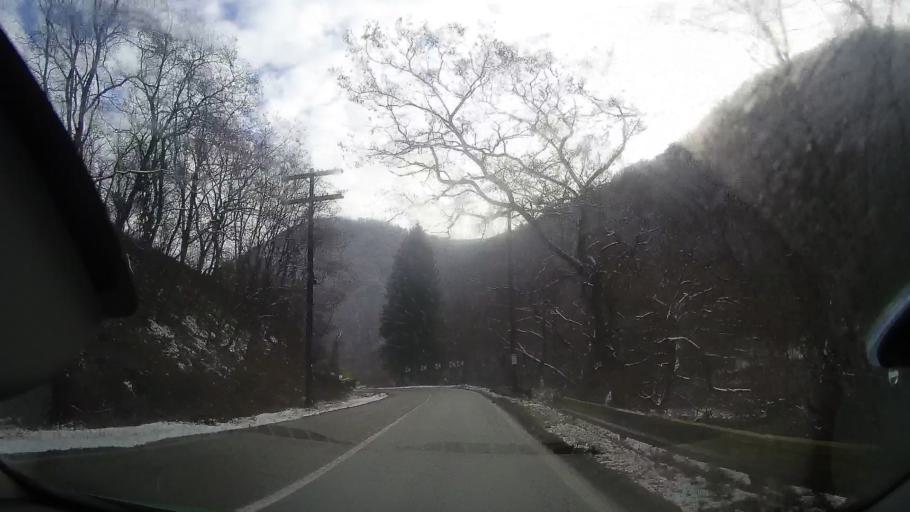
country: RO
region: Alba
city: Salciua de Sus
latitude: 46.3996
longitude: 23.3647
